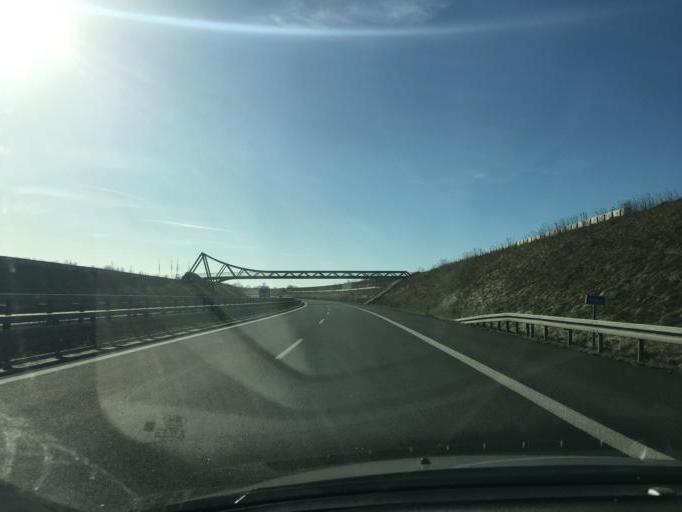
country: DE
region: Saxony
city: Frohburg
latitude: 51.0832
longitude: 12.5385
